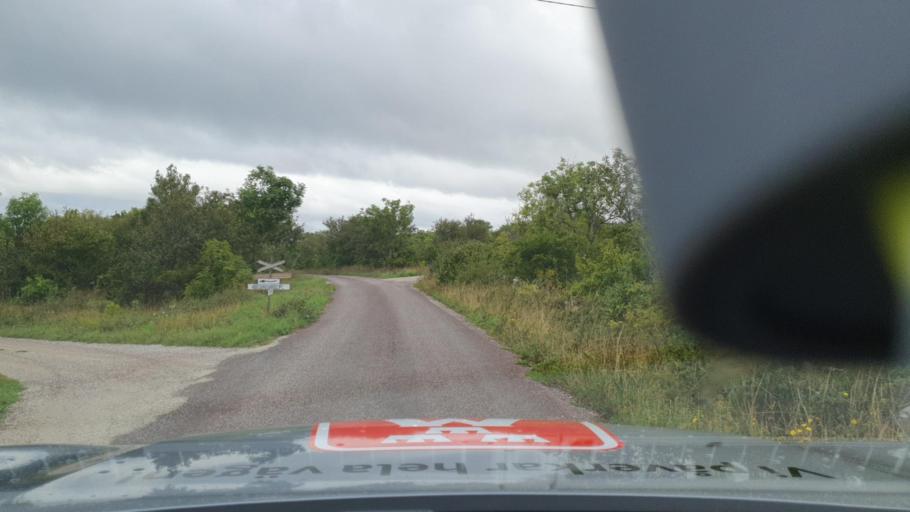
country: SE
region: Gotland
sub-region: Gotland
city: Hemse
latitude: 56.9569
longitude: 18.1761
